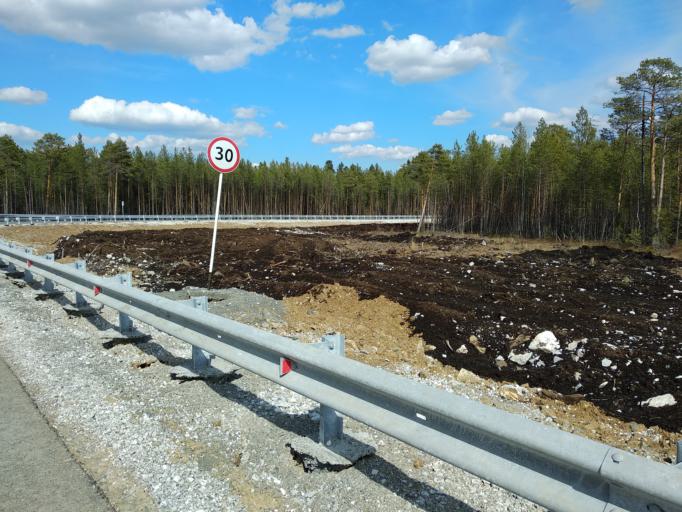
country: RU
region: Sverdlovsk
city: Krasnotur'insk
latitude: 59.7013
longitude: 60.1983
